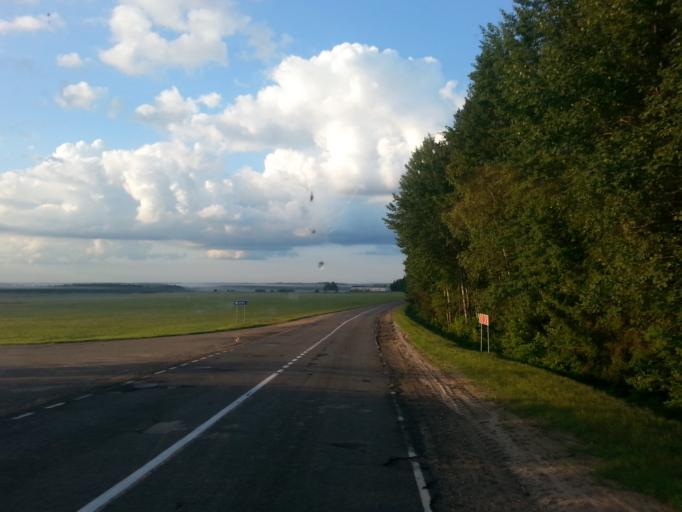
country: BY
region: Minsk
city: Il'ya
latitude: 54.5609
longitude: 27.2123
